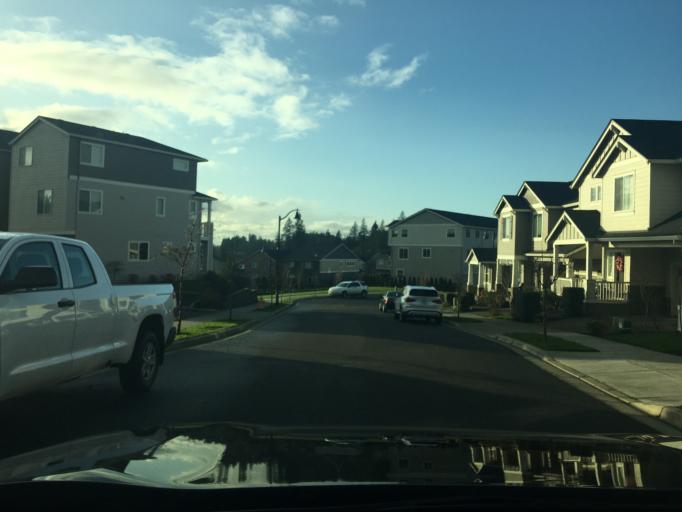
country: US
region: Oregon
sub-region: Washington County
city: Bethany
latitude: 45.5752
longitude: -122.8539
